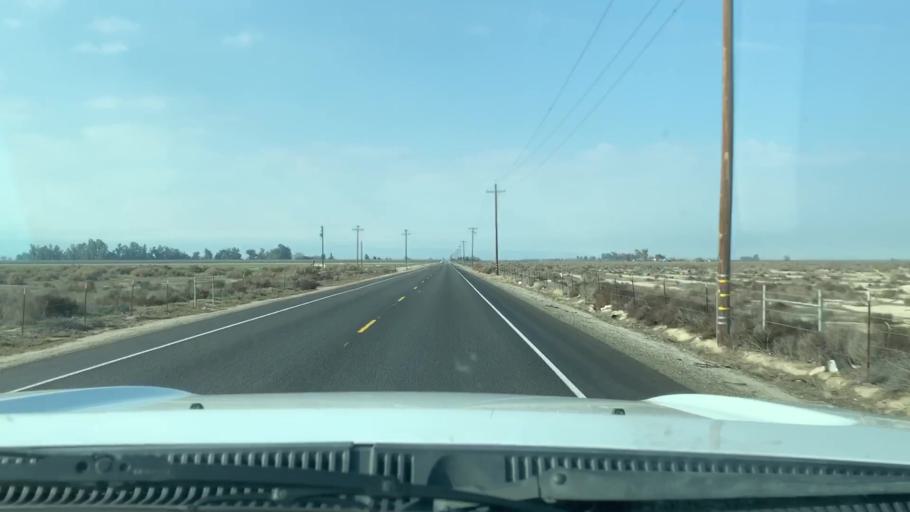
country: US
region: California
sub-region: Kern County
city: Buttonwillow
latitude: 35.4422
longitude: -119.3920
